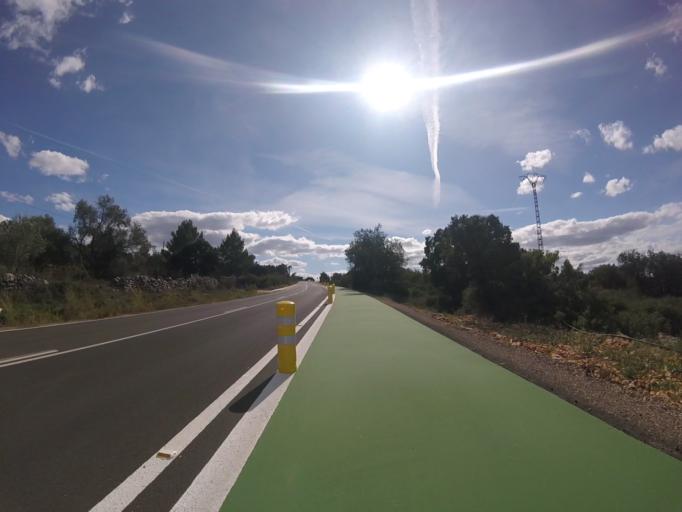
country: ES
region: Valencia
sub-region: Provincia de Castello
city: Albocasser
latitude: 40.4120
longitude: 0.0711
